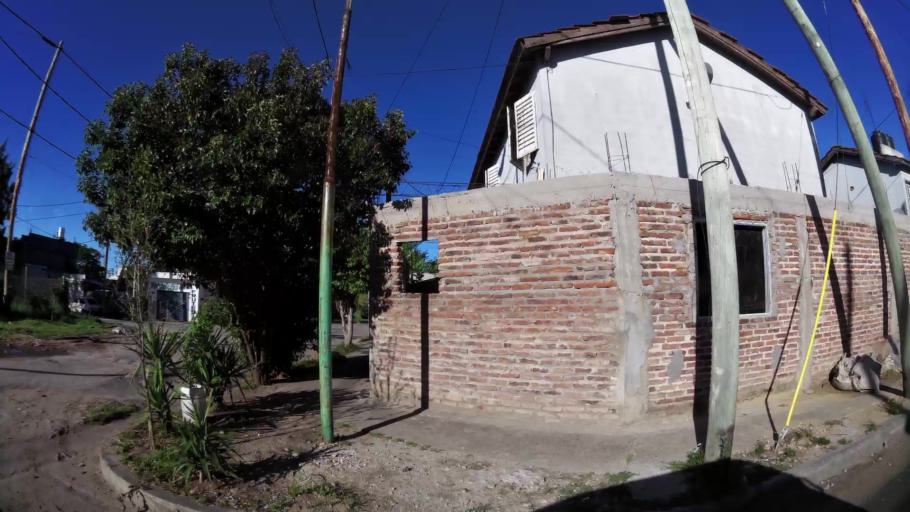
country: AR
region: Buenos Aires
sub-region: Partido de Lanus
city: Lanus
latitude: -34.7431
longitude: -58.3324
